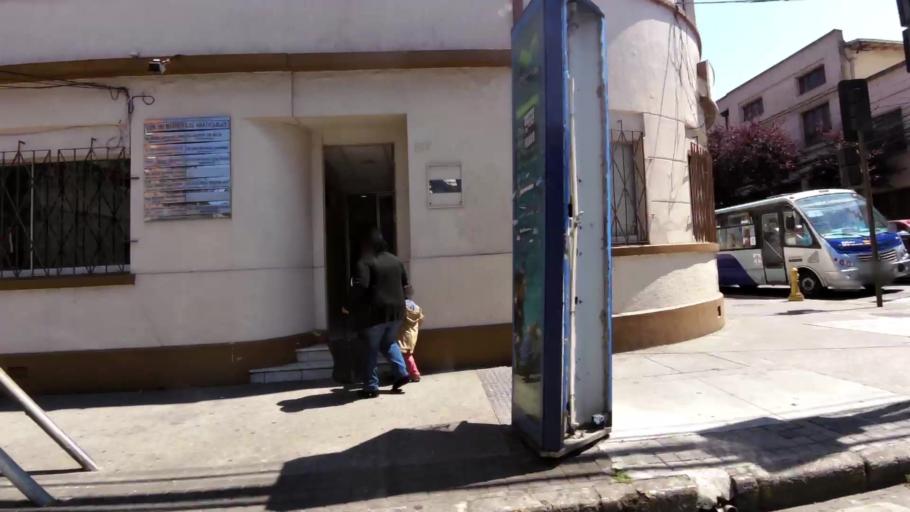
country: CL
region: Biobio
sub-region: Provincia de Concepcion
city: Concepcion
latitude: -36.8279
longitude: -73.0474
